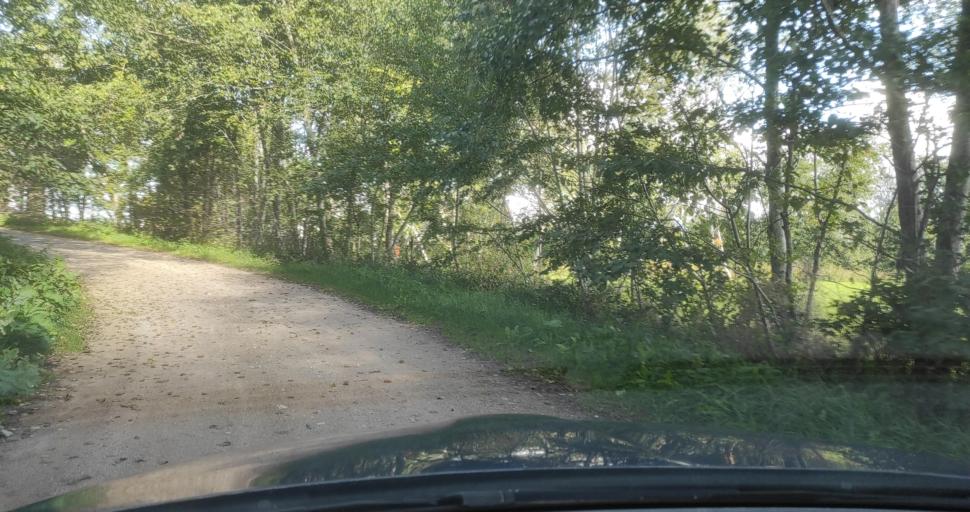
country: LV
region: Ventspils
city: Ventspils
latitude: 57.3684
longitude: 21.6318
